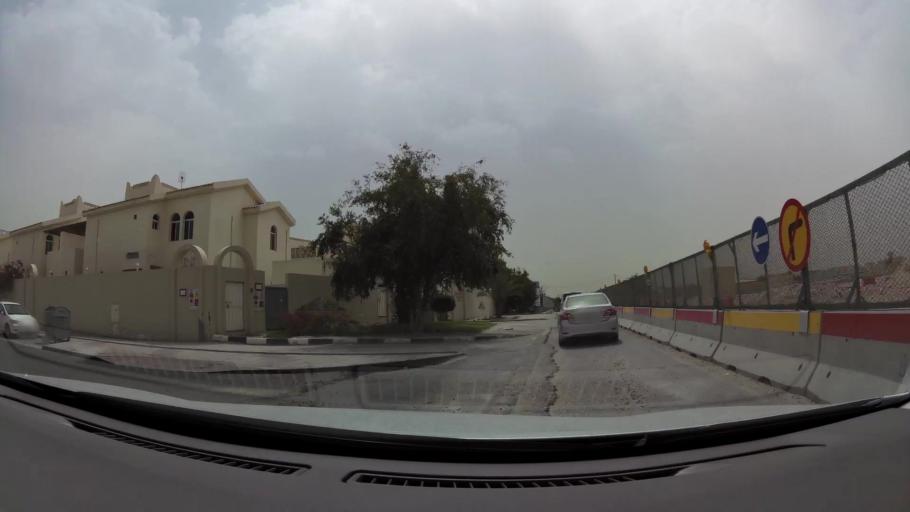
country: QA
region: Baladiyat ad Dawhah
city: Doha
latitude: 25.2662
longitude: 51.5036
